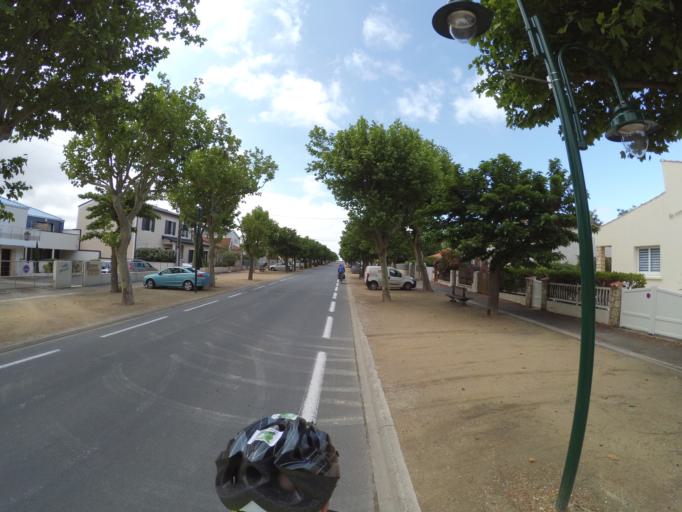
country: FR
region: Poitou-Charentes
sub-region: Departement de la Charente-Maritime
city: Chatelaillon-Plage
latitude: 46.0654
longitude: -1.0915
